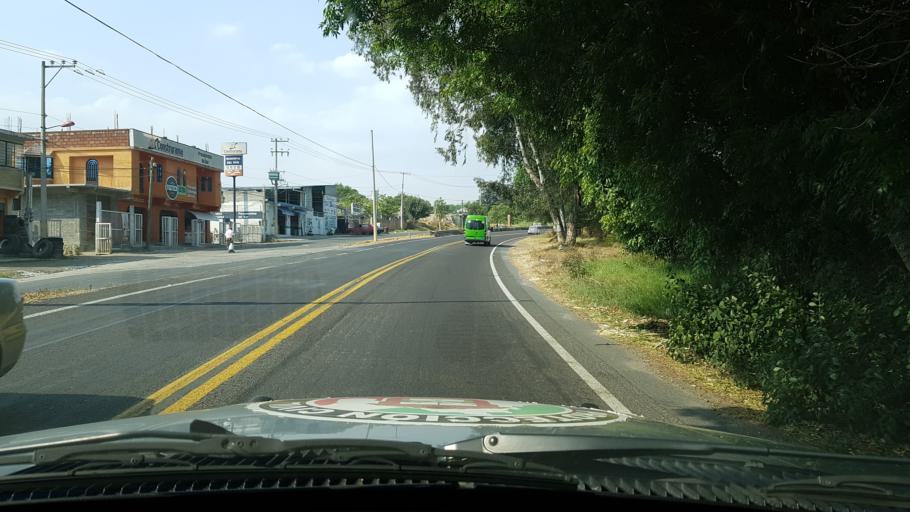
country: MX
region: Mexico
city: Tepetlixpa
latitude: 19.0214
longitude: -98.8245
